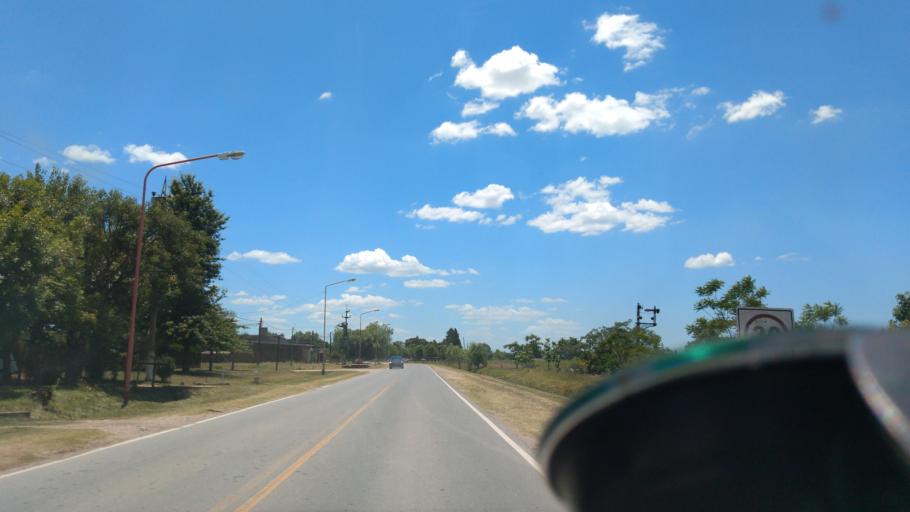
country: AR
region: Santa Fe
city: Laguna Paiva
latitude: -31.3163
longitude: -60.6585
